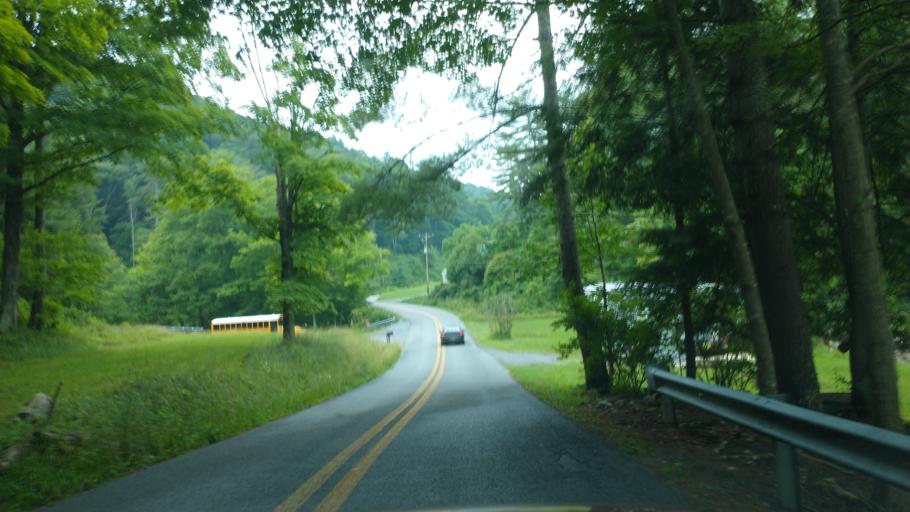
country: US
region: West Virginia
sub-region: Mercer County
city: Athens
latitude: 37.4286
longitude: -80.9836
